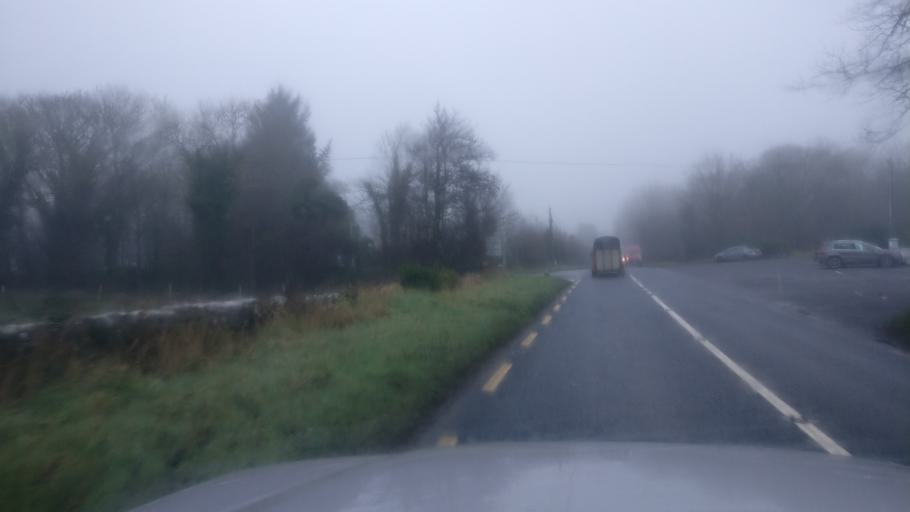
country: IE
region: Connaught
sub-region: County Galway
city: Loughrea
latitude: 53.1663
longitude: -8.6758
